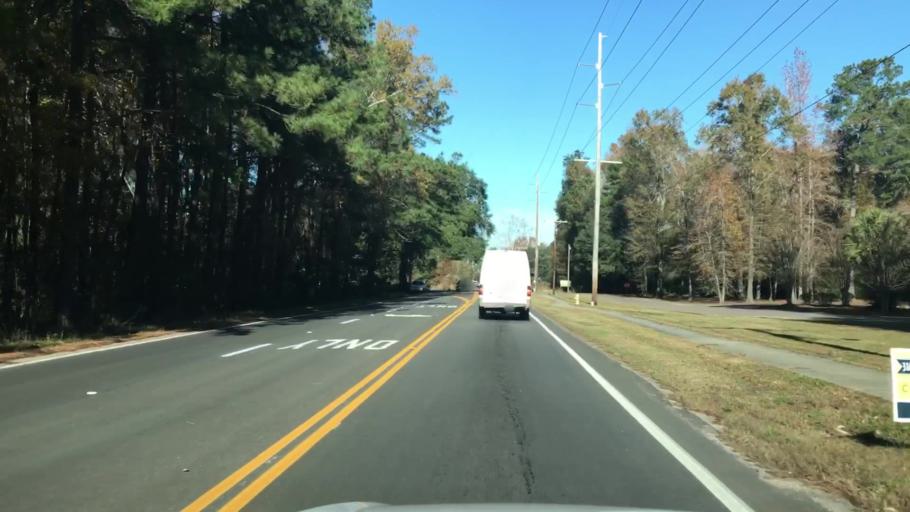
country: US
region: South Carolina
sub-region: Dorchester County
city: Summerville
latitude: 33.0021
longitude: -80.2323
